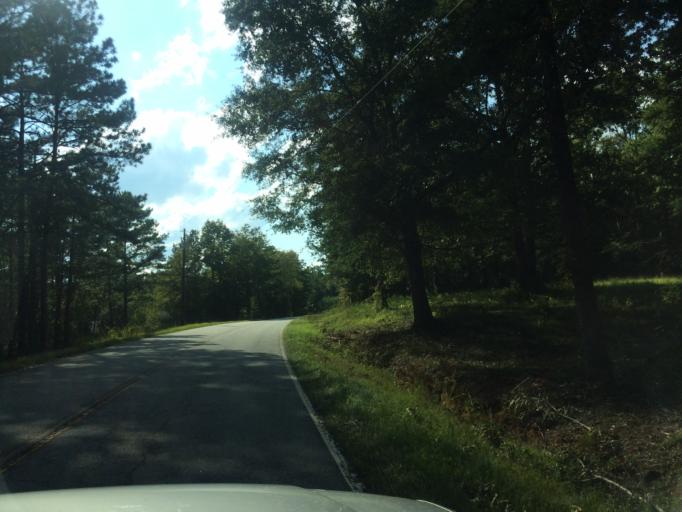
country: US
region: South Carolina
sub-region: Greenwood County
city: Ware Shoals
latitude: 34.4633
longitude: -82.1695
